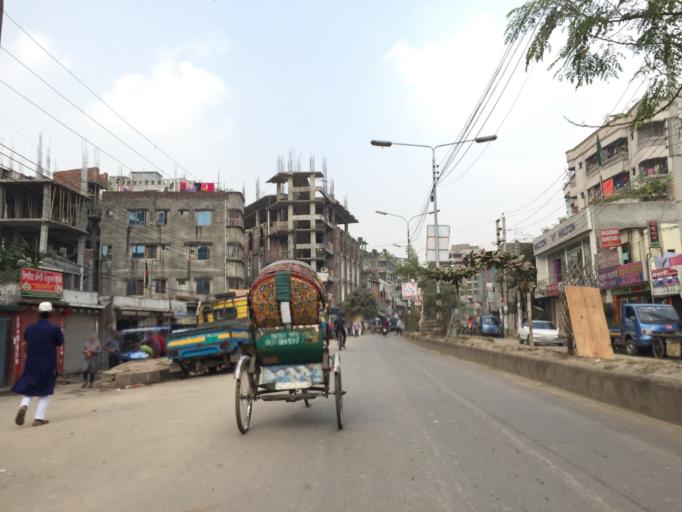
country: BD
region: Dhaka
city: Azimpur
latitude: 23.7913
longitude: 90.3657
